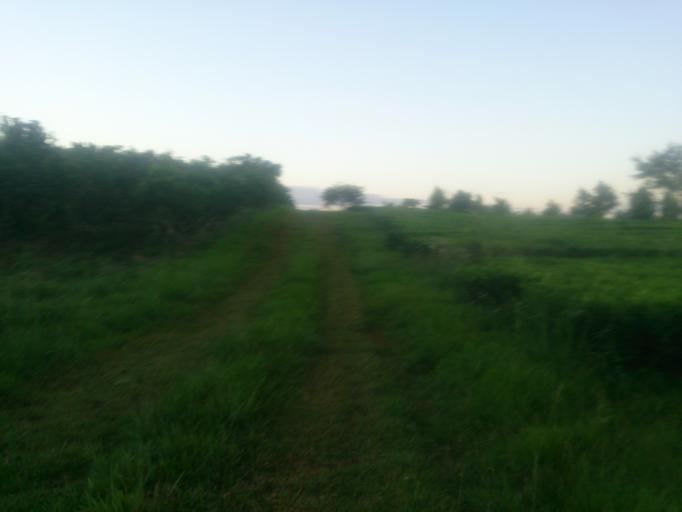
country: AR
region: Misiones
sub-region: Departamento de Obera
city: Obera
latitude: -27.4448
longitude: -55.0920
